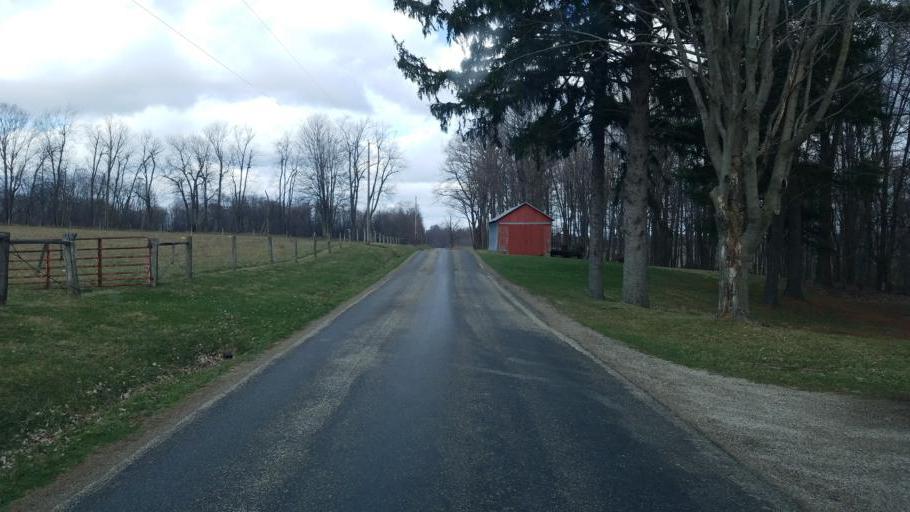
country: US
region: Ohio
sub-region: Sandusky County
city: Bellville
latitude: 40.6591
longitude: -82.4446
